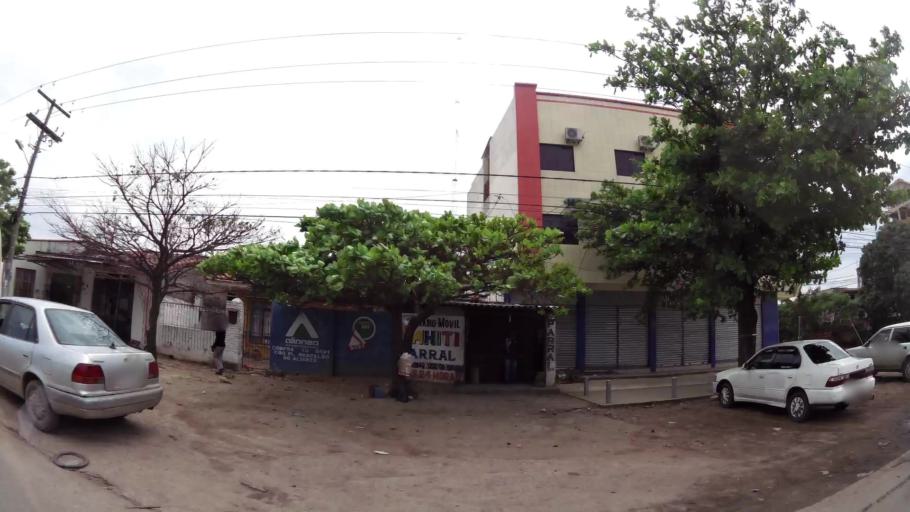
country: BO
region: Santa Cruz
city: Santa Cruz de la Sierra
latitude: -17.7607
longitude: -63.1639
